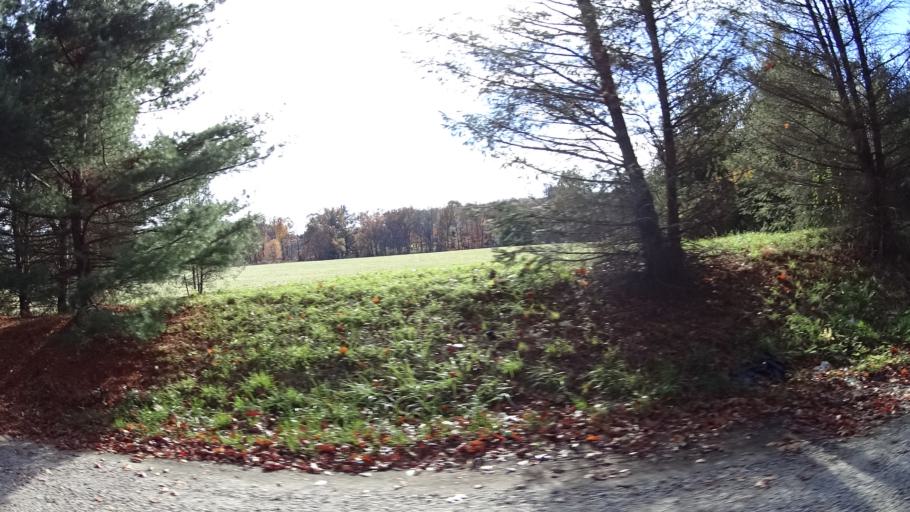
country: US
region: New Jersey
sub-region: Morris County
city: Morristown
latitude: 40.7479
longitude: -74.5089
